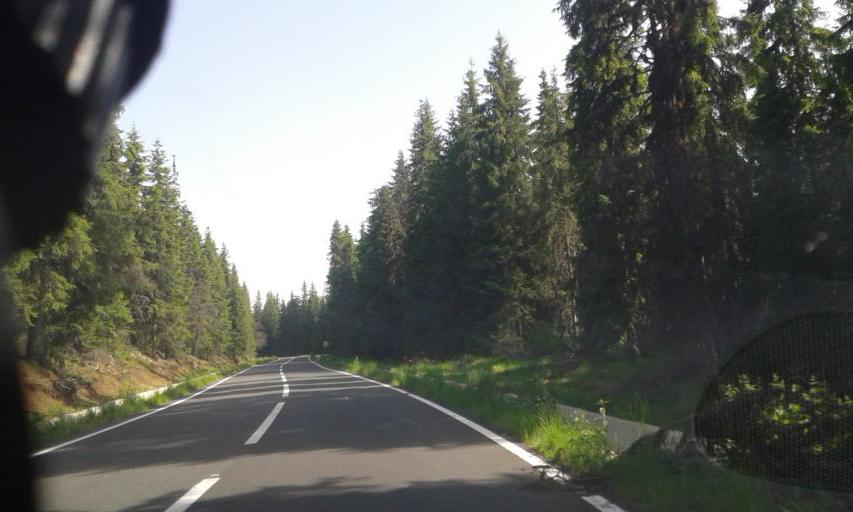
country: RO
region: Hunedoara
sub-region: Oras Petrila
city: Petrila
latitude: 45.4901
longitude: 23.6374
